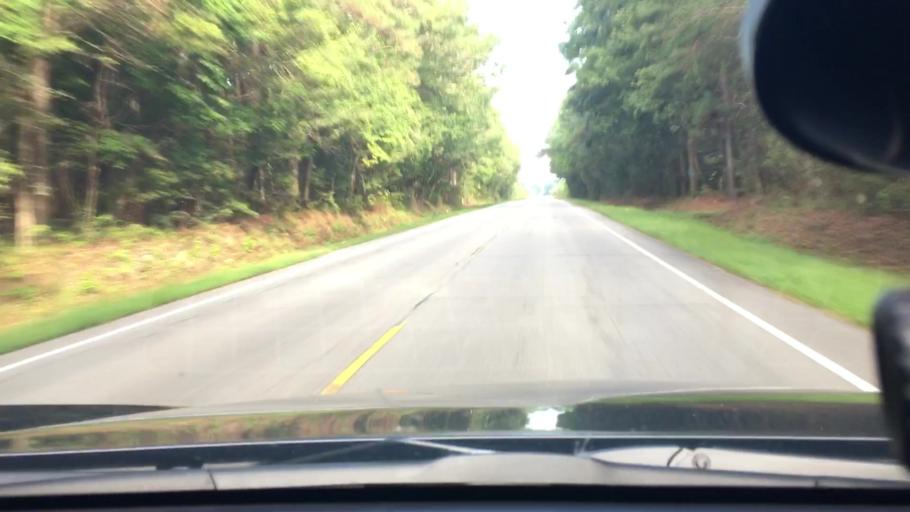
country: US
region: North Carolina
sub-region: Edgecombe County
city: Pinetops
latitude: 35.7674
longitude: -77.5662
